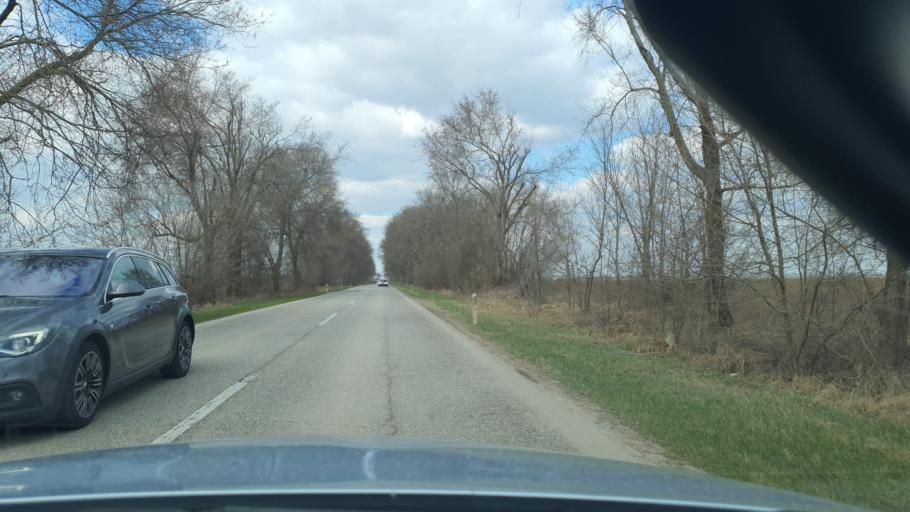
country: RS
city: Obrovac
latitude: 45.4372
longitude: 19.3746
